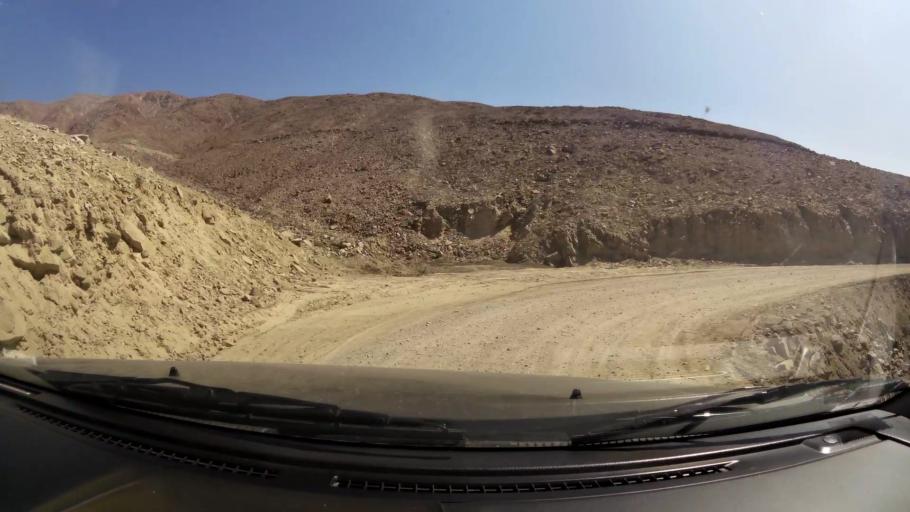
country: PE
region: Ica
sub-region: Provincia de Ica
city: Guadalupe
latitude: -13.8945
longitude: -75.6588
